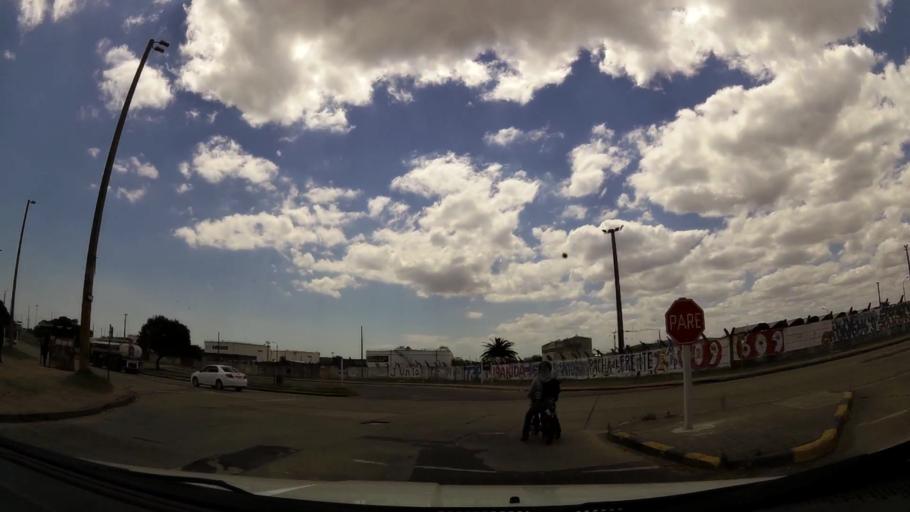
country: UY
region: Canelones
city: La Paz
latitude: -34.8228
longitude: -56.2414
